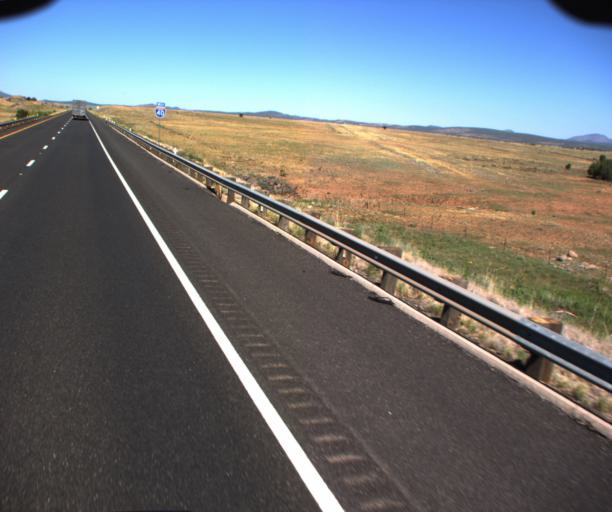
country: US
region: Arizona
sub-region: Yavapai County
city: Paulden
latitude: 35.2310
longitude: -112.5940
